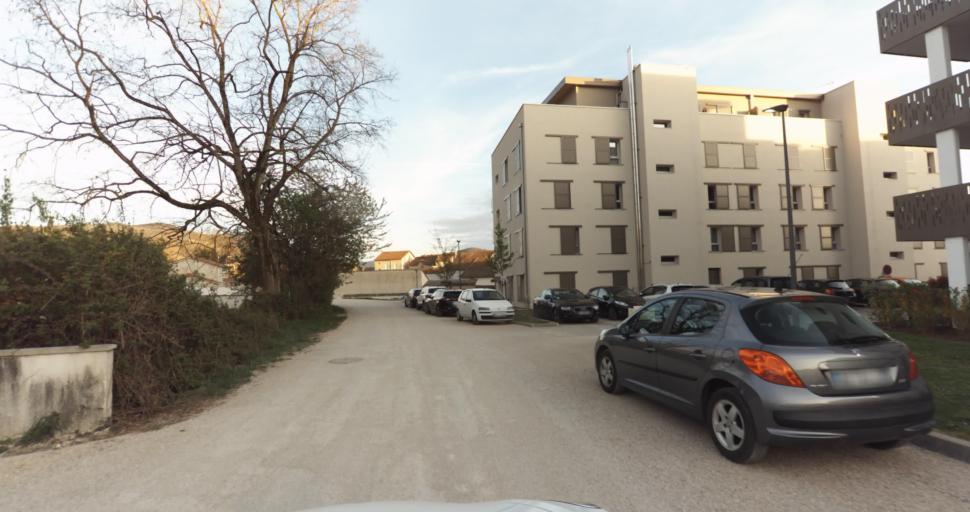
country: FR
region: Rhone-Alpes
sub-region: Departement de l'Ain
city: Amberieu-en-Bugey
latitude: 45.9595
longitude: 5.3533
